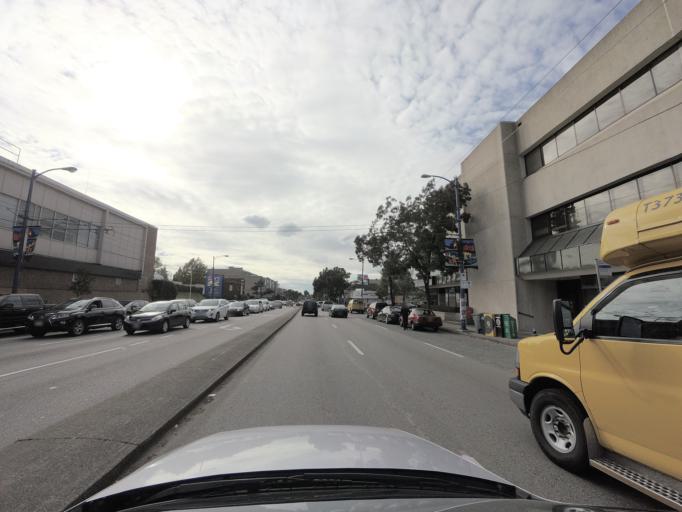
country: CA
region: British Columbia
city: Burnaby
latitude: 49.2322
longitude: -123.0262
